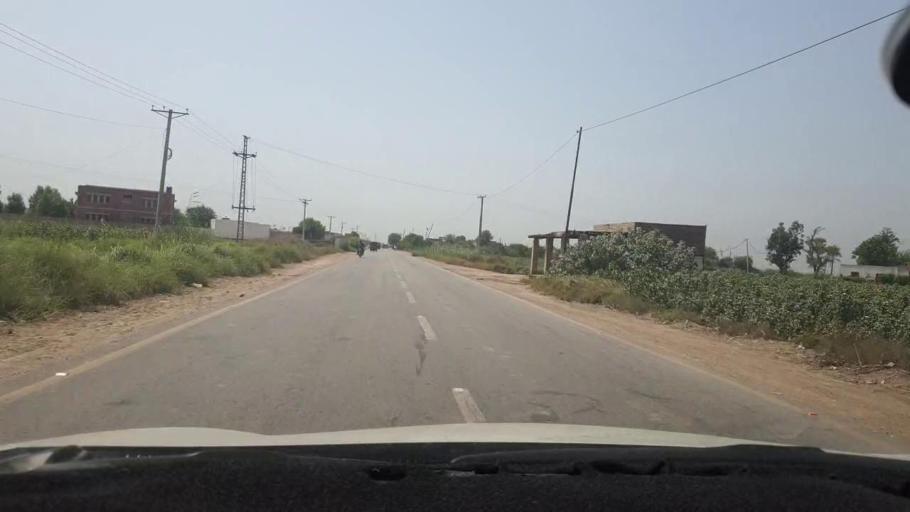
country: PK
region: Sindh
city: Shahdadpur
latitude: 25.8992
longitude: 68.5890
